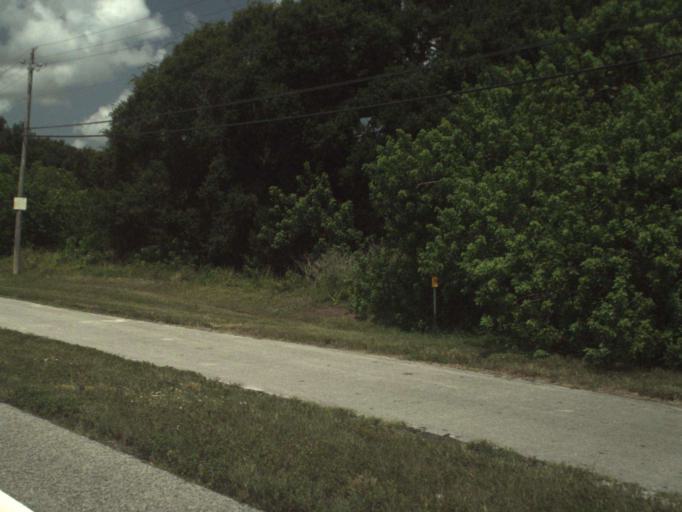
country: US
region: Florida
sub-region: Saint Lucie County
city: Fort Pierce South
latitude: 27.4102
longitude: -80.4182
